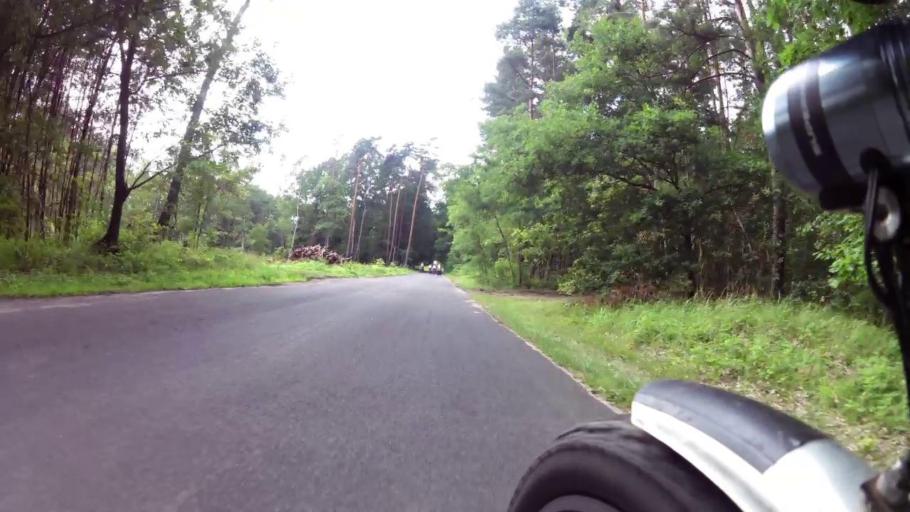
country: PL
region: West Pomeranian Voivodeship
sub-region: Powiat mysliborski
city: Debno
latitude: 52.7882
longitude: 14.6767
